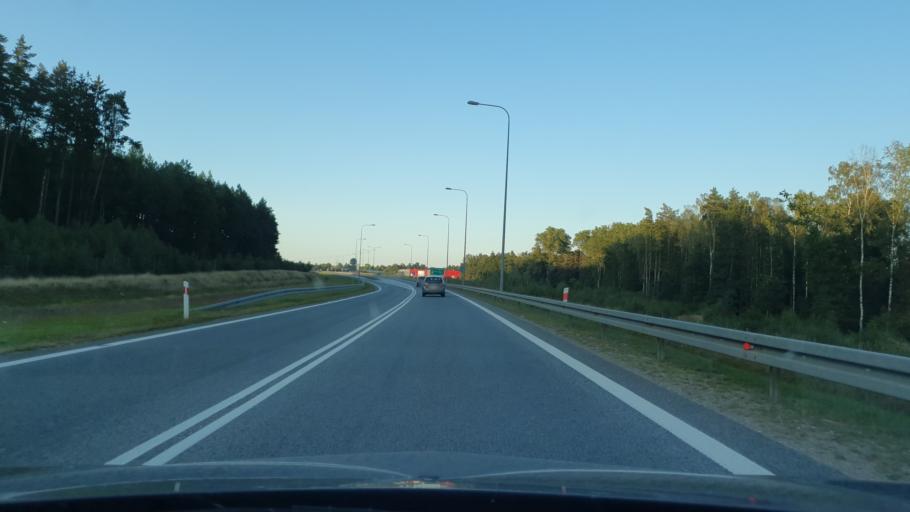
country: PL
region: Pomeranian Voivodeship
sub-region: Slupsk
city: Slupsk
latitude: 54.4423
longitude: 17.0766
